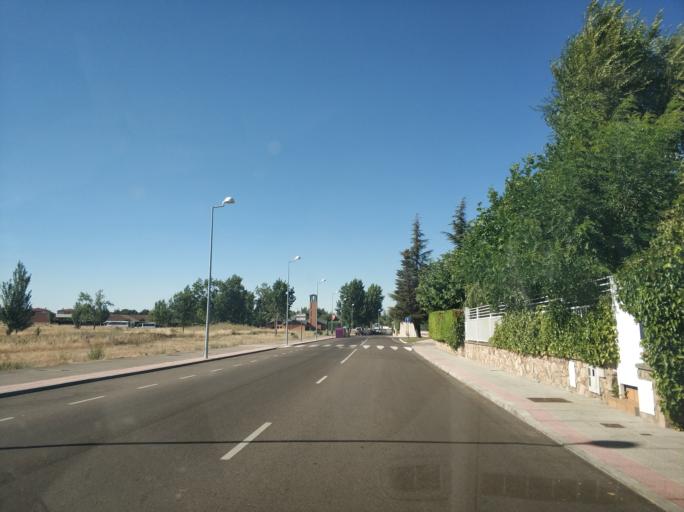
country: ES
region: Castille and Leon
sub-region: Provincia de Salamanca
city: Santa Marta de Tormes
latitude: 40.9354
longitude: -5.6254
